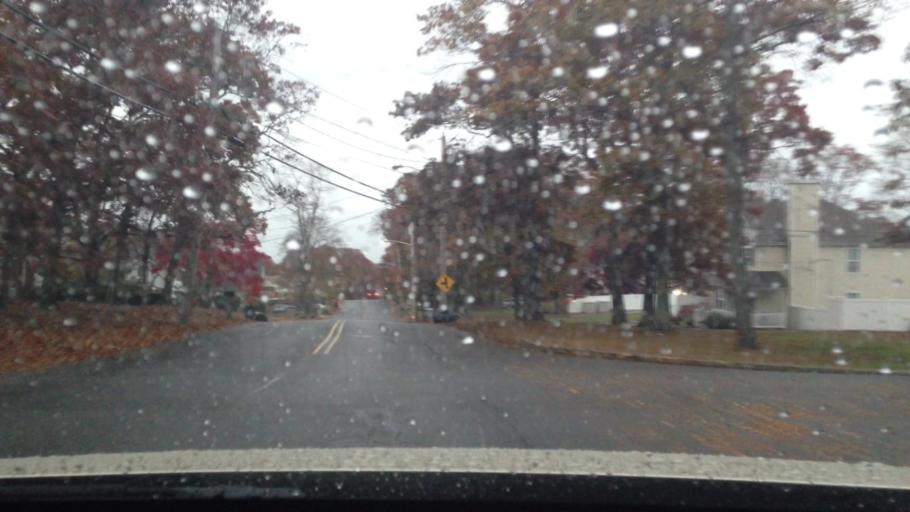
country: US
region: New York
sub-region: Suffolk County
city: Selden
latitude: 40.8503
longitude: -73.0331
